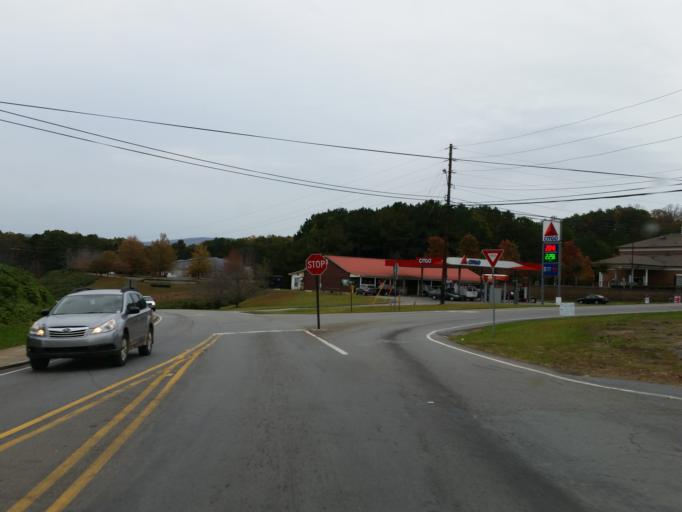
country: US
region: Georgia
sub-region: Pickens County
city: Jasper
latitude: 34.4719
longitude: -84.4229
